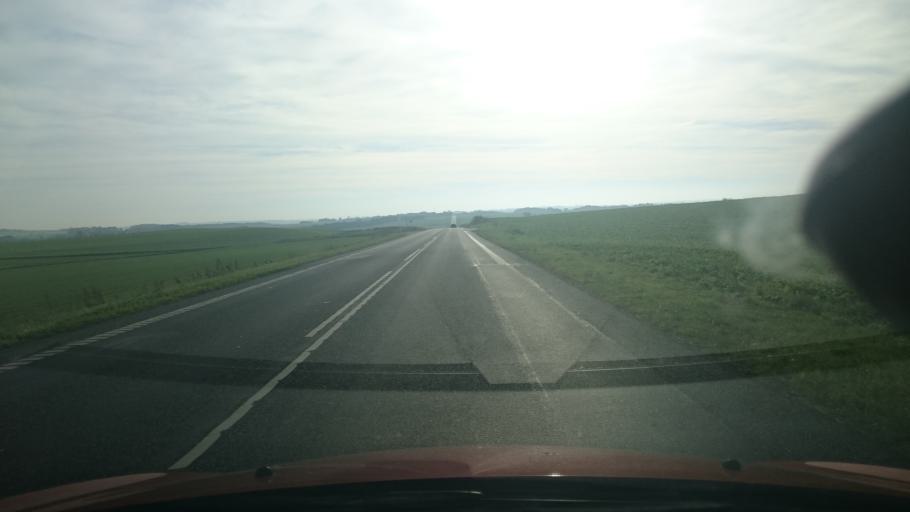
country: DK
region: Central Jutland
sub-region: Randers Kommune
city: Assentoft
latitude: 56.4252
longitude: 10.2029
